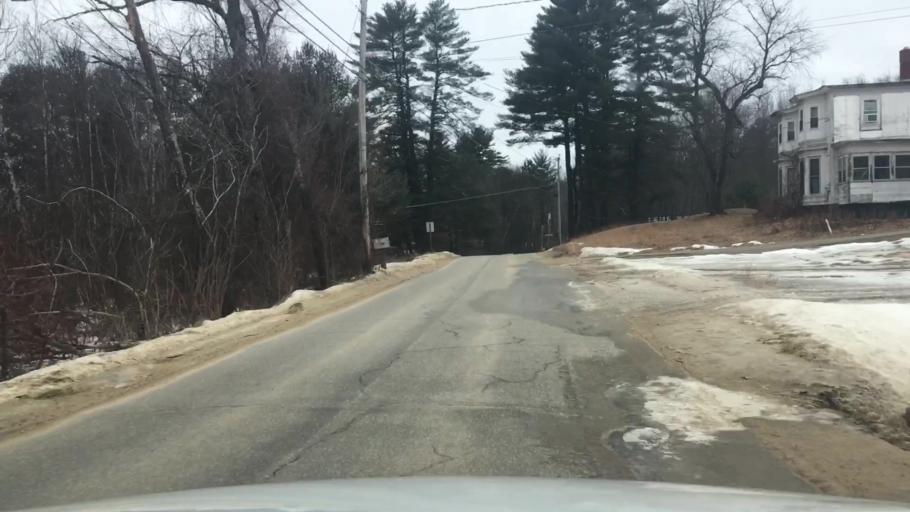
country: US
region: New Hampshire
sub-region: Strafford County
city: Rochester
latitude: 43.3475
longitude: -70.9616
